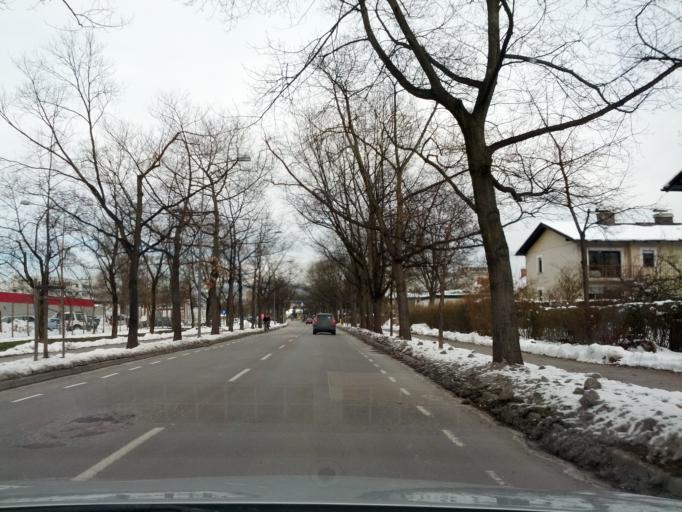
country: SI
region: Ljubljana
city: Ljubljana
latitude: 46.0797
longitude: 14.5068
